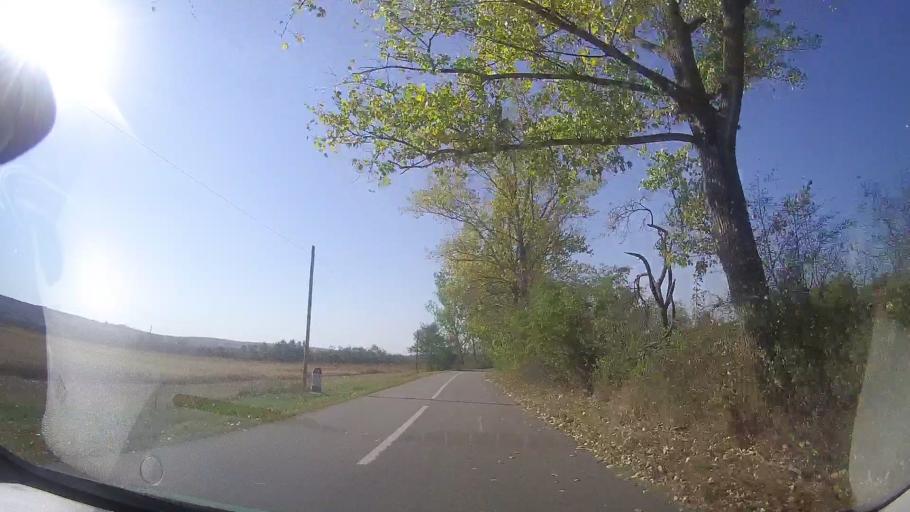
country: RO
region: Timis
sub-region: Comuna Secas
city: Secas
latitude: 45.8576
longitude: 21.8024
